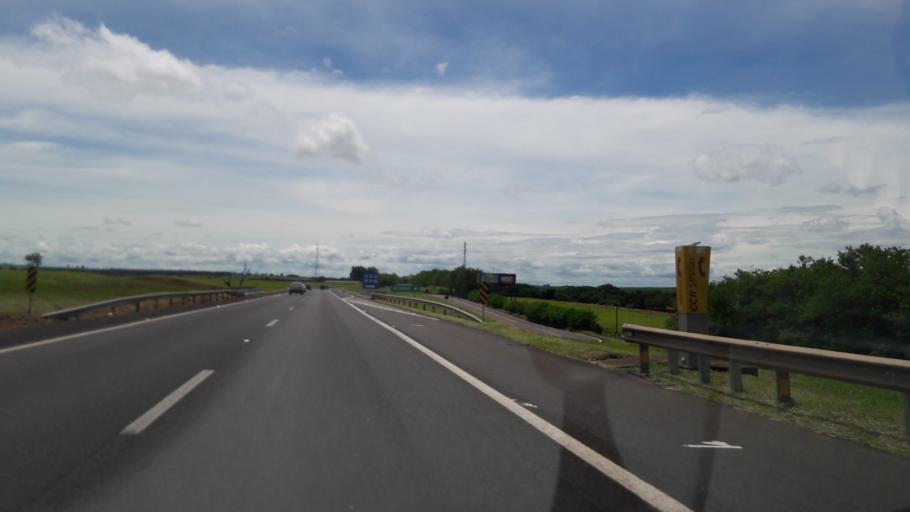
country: BR
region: Sao Paulo
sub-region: Avare
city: Avare
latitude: -22.9568
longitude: -48.8509
